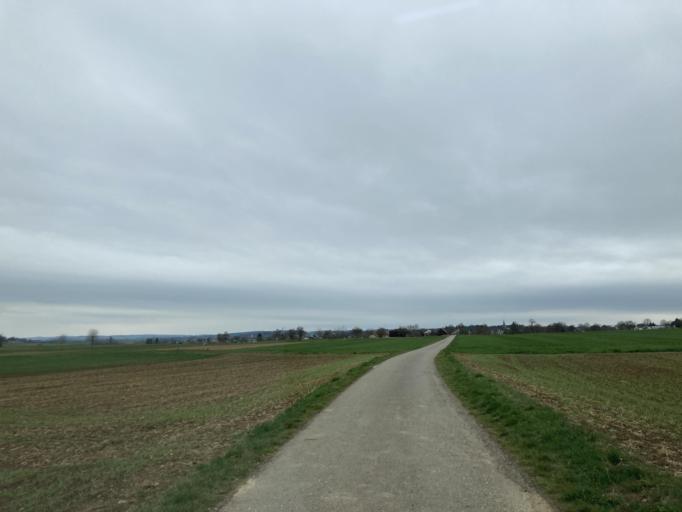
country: DE
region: Baden-Wuerttemberg
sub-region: Regierungsbezirk Stuttgart
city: Motzingen
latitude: 48.5039
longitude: 8.7911
